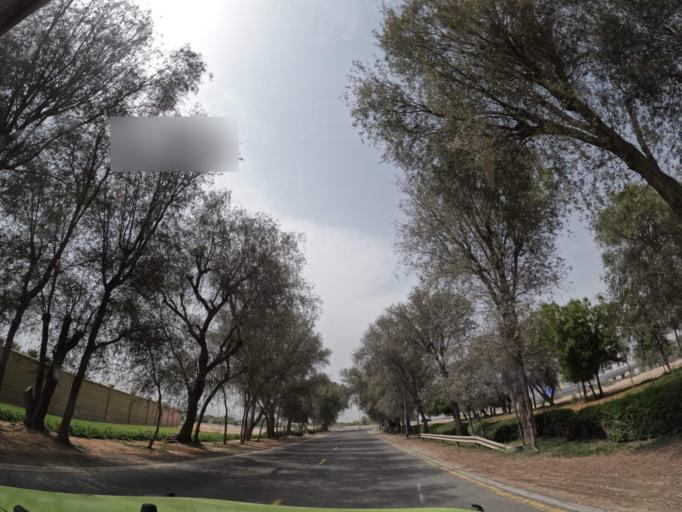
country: AE
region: Dubai
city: Dubai
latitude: 25.1484
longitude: 55.3379
